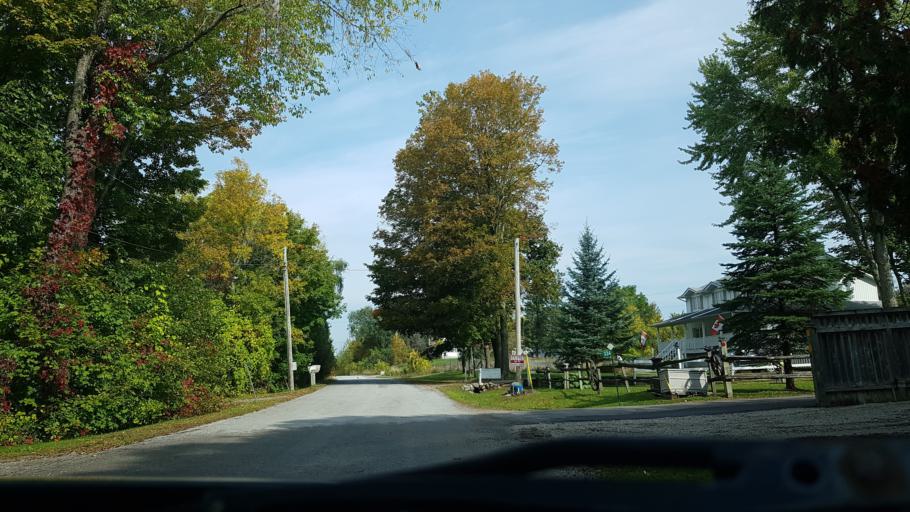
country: CA
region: Ontario
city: Orillia
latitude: 44.6673
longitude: -79.0965
